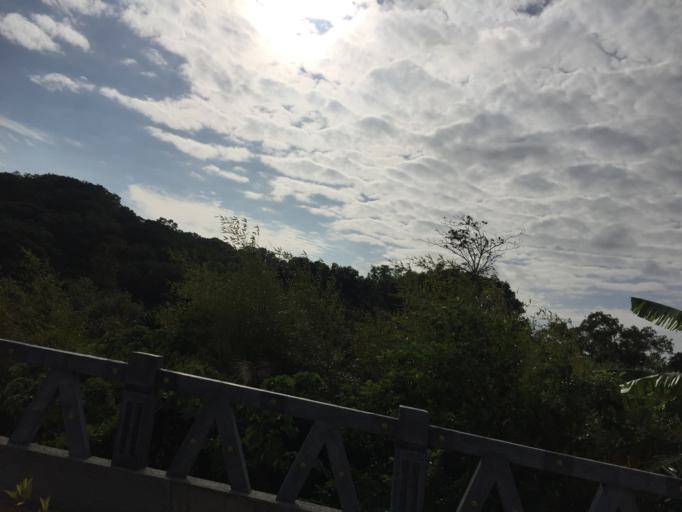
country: TW
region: Taiwan
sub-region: Hsinchu
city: Hsinchu
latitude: 24.7745
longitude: 120.9491
